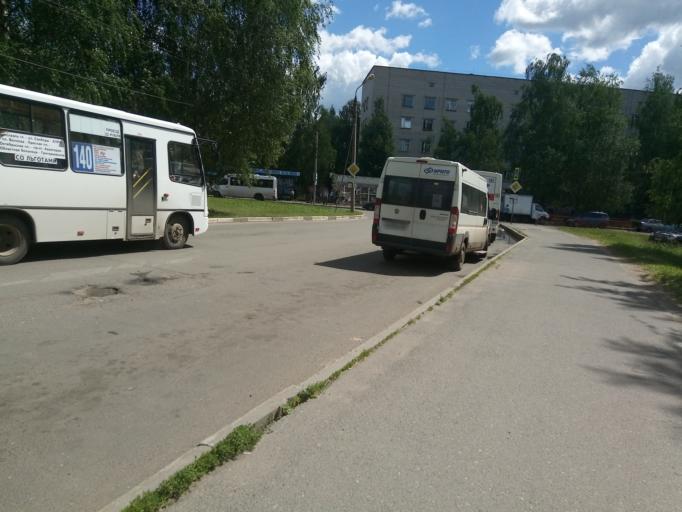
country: RU
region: Jaroslavl
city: Yaroslavl
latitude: 57.6573
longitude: 39.9673
